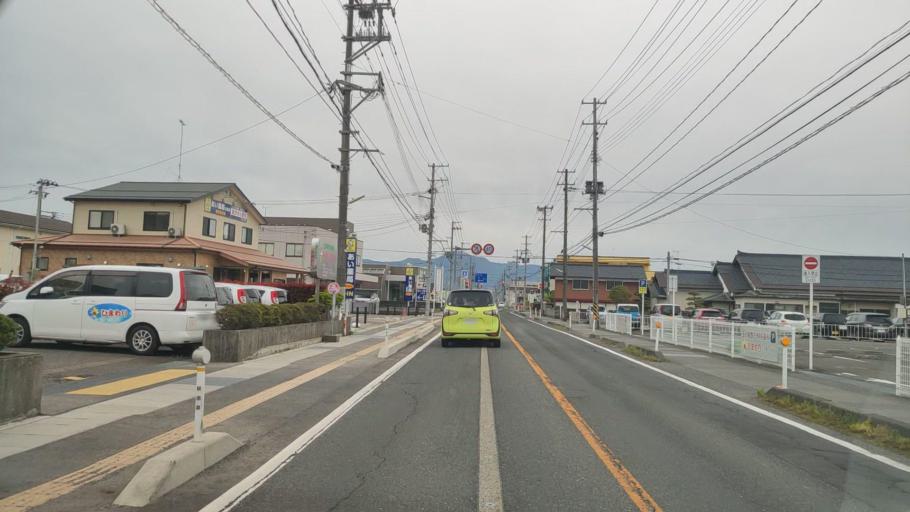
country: JP
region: Niigata
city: Gosen
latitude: 37.7308
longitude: 139.1770
